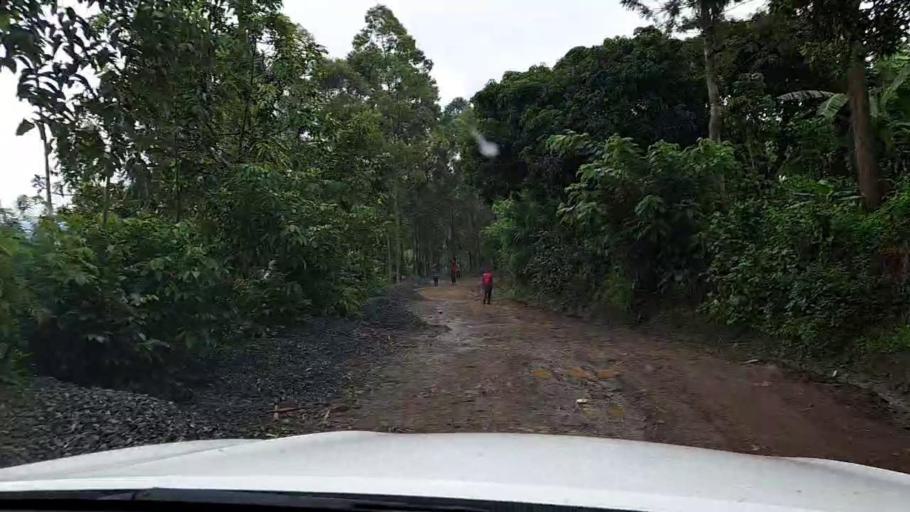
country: RW
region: Western Province
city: Cyangugu
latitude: -2.5449
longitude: 29.0376
